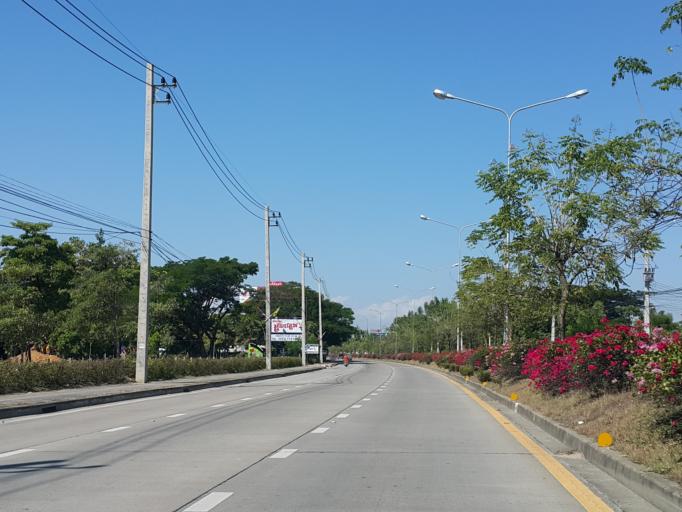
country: TH
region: Chiang Mai
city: San Sai
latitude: 18.8359
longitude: 99.0021
